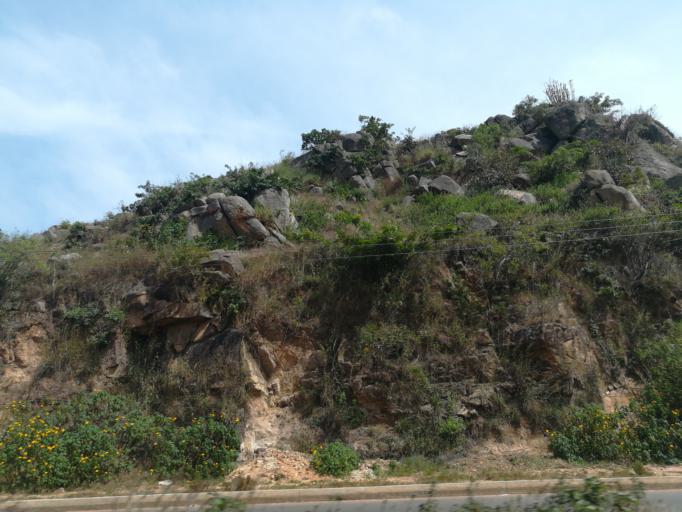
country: NG
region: Plateau
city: Bukuru
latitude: 9.8310
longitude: 8.8671
